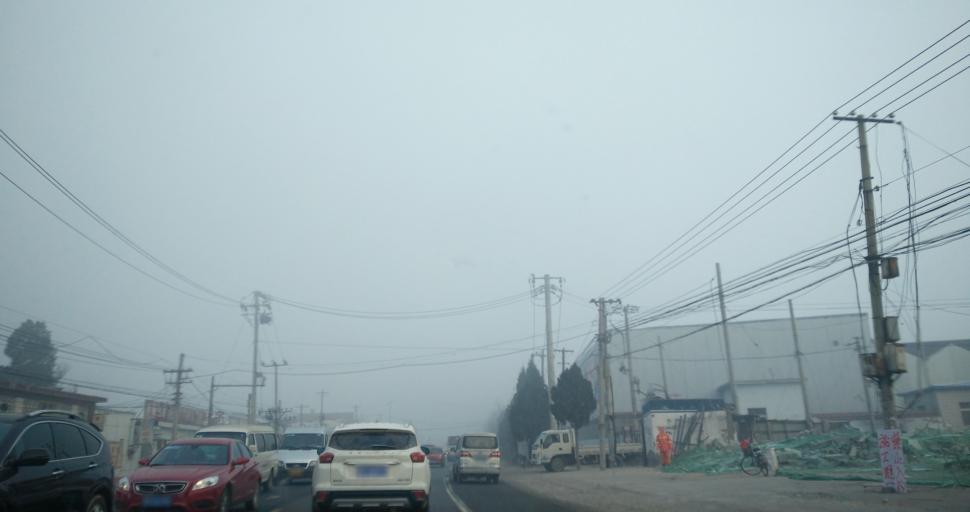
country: CN
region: Beijing
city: Yinghai
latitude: 39.7283
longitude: 116.4566
